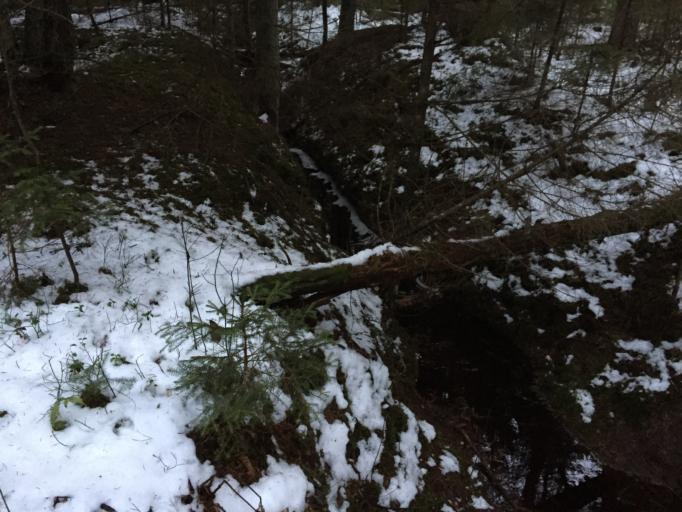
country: LV
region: Garkalne
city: Garkalne
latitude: 56.9648
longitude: 24.4713
